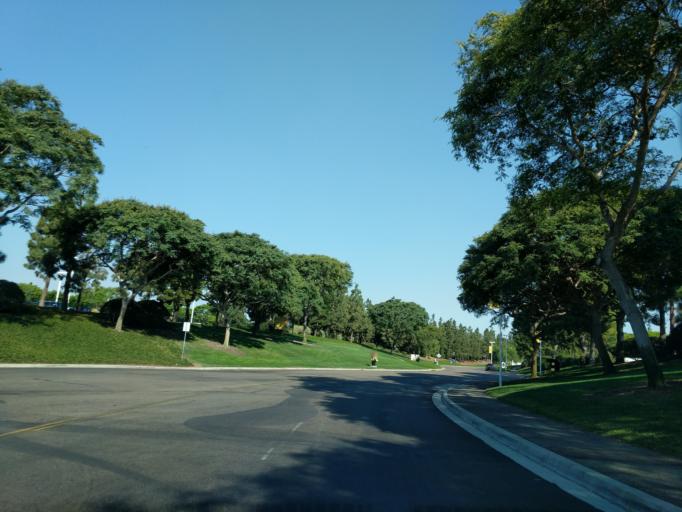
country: US
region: California
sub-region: San Diego County
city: Carlsbad
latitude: 33.1261
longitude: -117.3142
